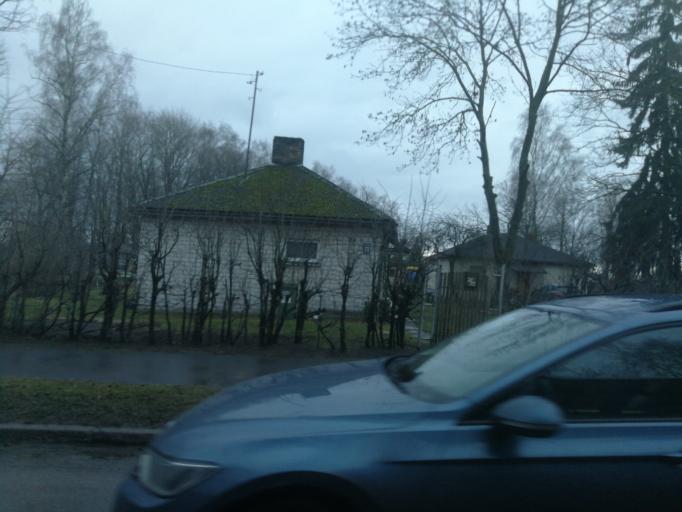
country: LV
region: Riga
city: Bolderaja
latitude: 57.0519
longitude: 24.0673
